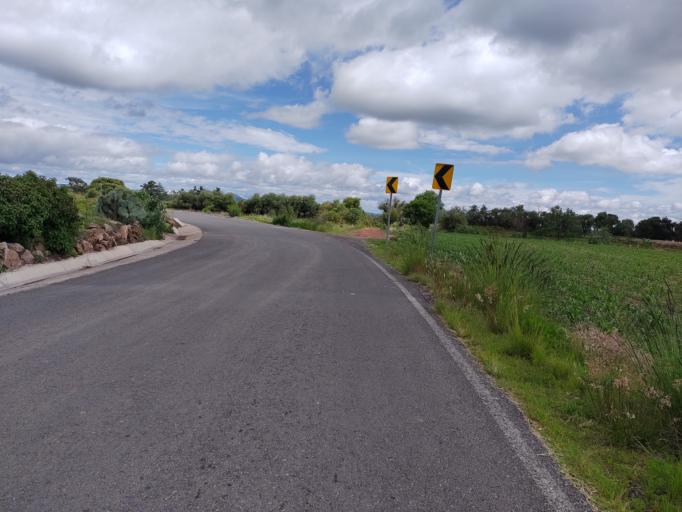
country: MX
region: Mexico
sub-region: Aculco
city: Gunyo Poniente (San Jose Gunyo)
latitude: 20.1186
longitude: -99.8780
